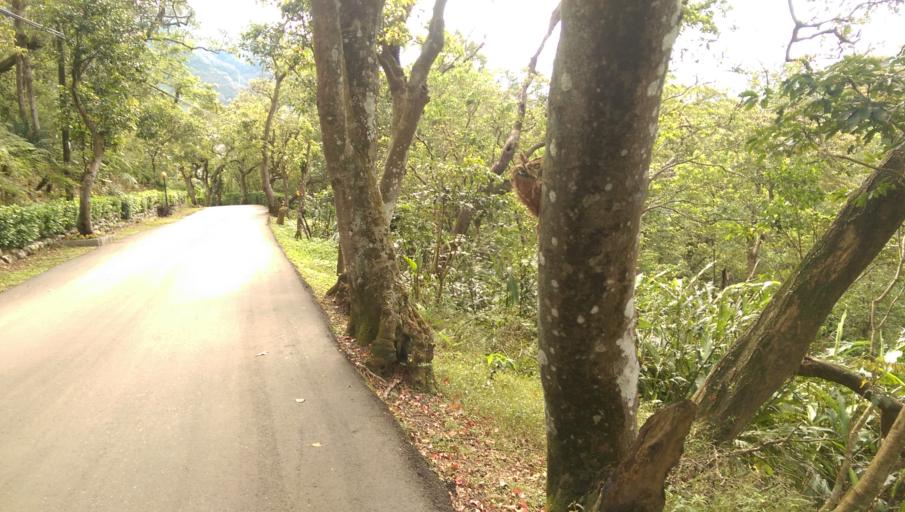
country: TW
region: Taipei
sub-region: Taipei
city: Banqiao
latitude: 24.9303
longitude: 121.5425
